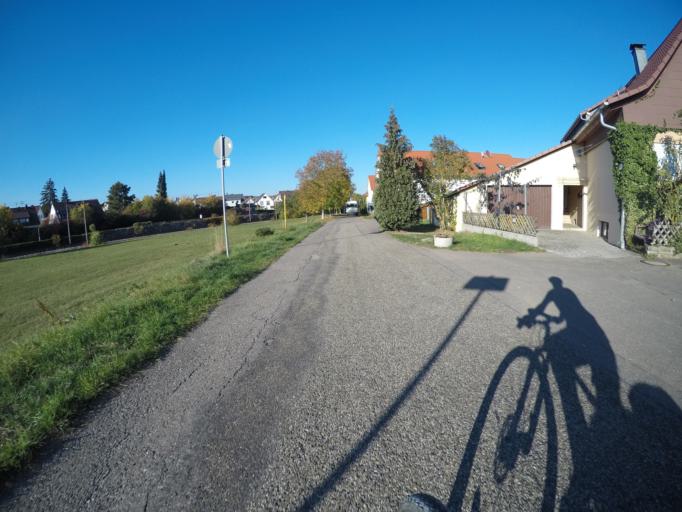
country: DE
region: Baden-Wuerttemberg
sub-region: Regierungsbezirk Stuttgart
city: Nufringen
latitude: 48.6163
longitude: 8.8849
